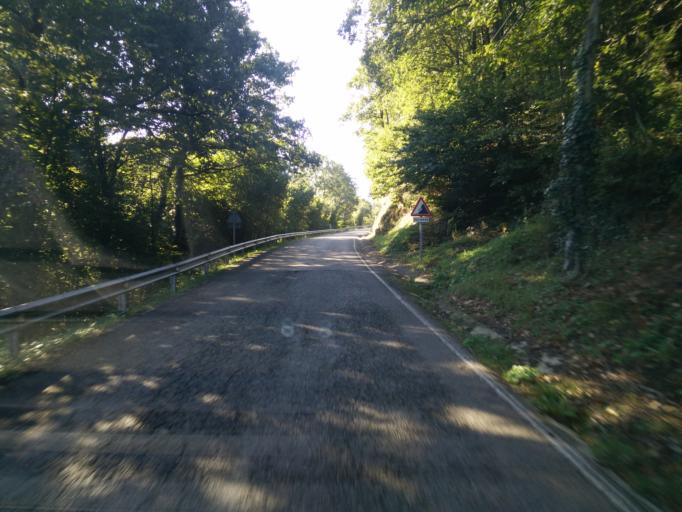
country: ES
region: Cantabria
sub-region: Provincia de Cantabria
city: San Pedro del Romeral
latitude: 43.1372
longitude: -3.8152
